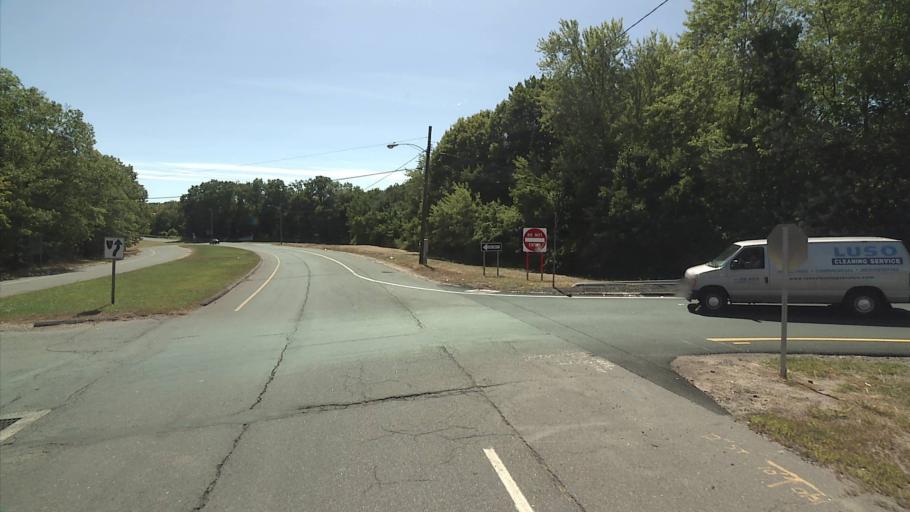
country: US
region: Connecticut
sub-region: New Haven County
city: Naugatuck
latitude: 41.5126
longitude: -73.0490
